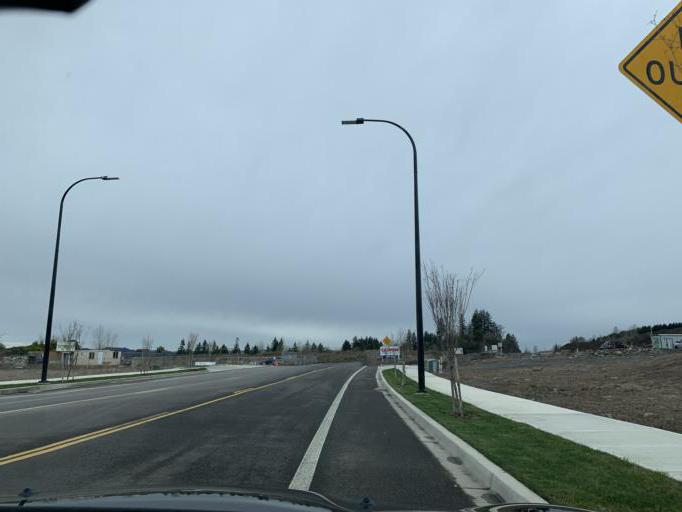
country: US
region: Washington
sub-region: Clark County
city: Mill Plain
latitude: 45.5868
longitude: -122.4747
